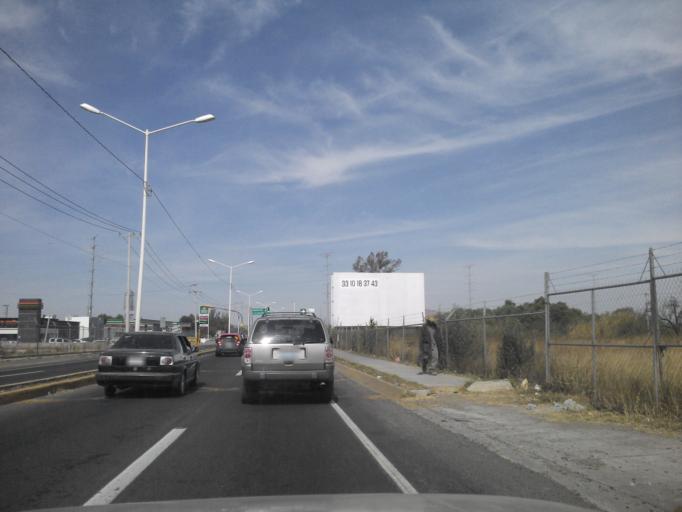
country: MX
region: Jalisco
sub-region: Tlajomulco de Zuniga
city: Hacienda los Fresnos
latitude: 20.5370
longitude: -103.4045
